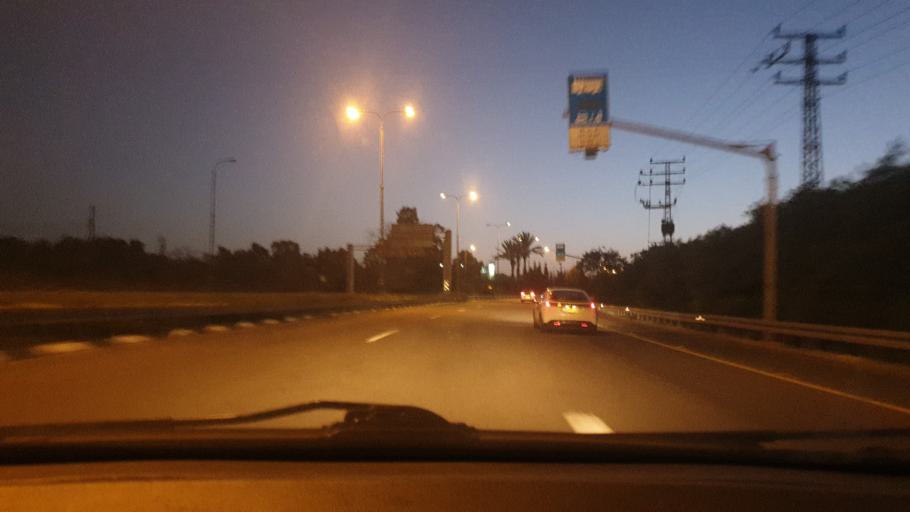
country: IL
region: Central District
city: Bet Dagan
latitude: 31.9979
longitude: 34.8187
